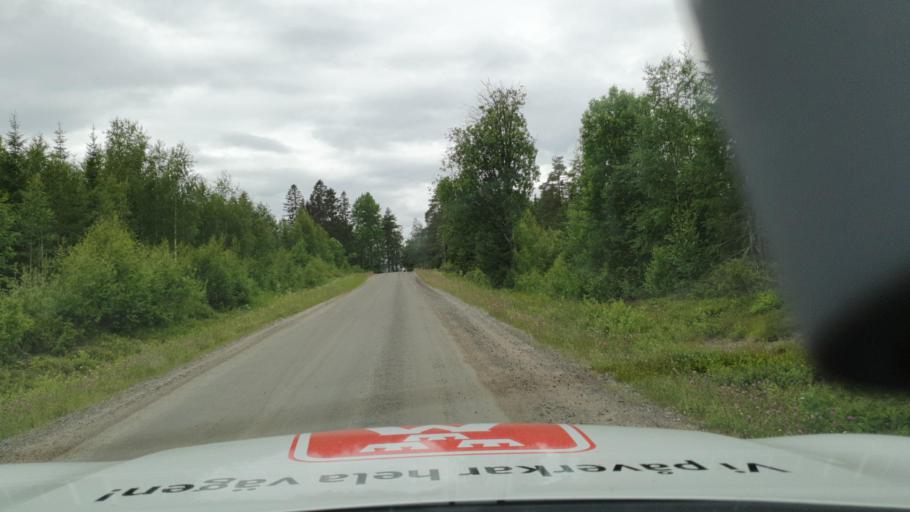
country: SE
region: Vaesterbotten
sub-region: Nordmalings Kommun
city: Nordmaling
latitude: 63.7164
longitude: 19.3347
